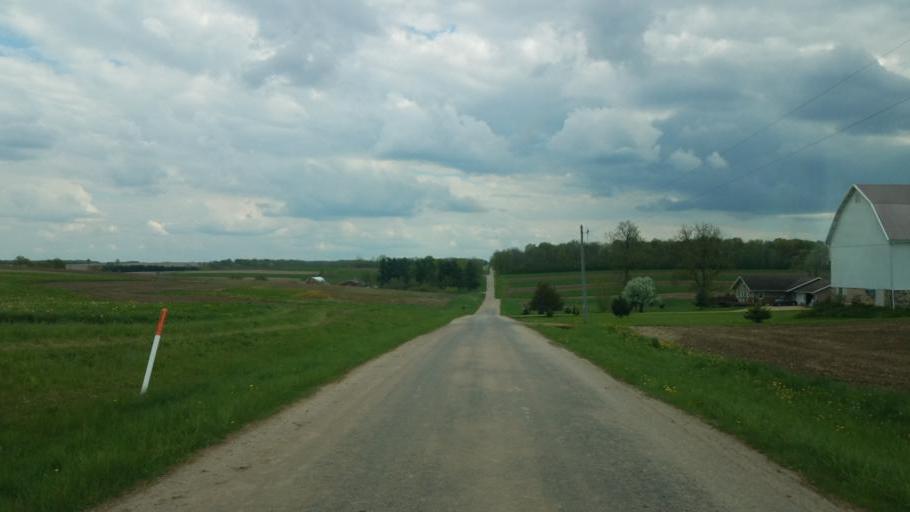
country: US
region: Wisconsin
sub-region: Vernon County
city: Hillsboro
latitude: 43.5889
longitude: -90.3318
